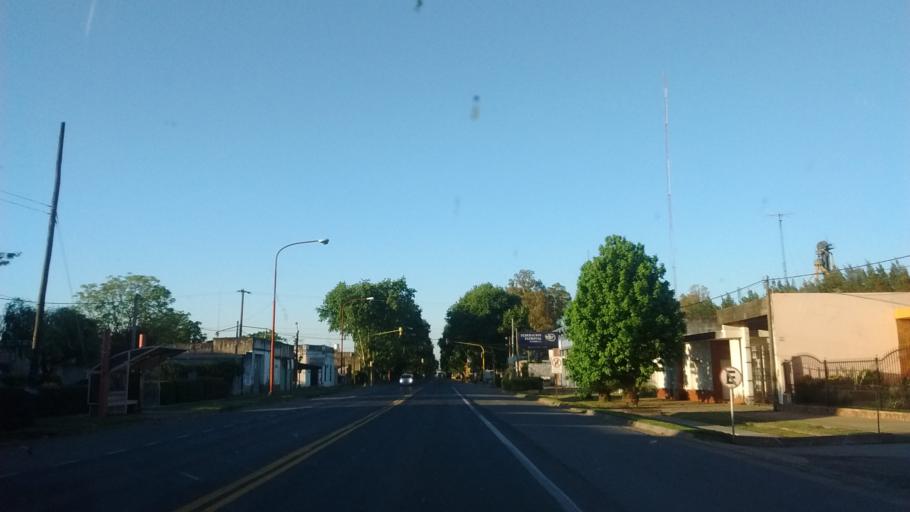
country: AR
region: Santa Fe
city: Firmat
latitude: -33.2405
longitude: -61.3554
